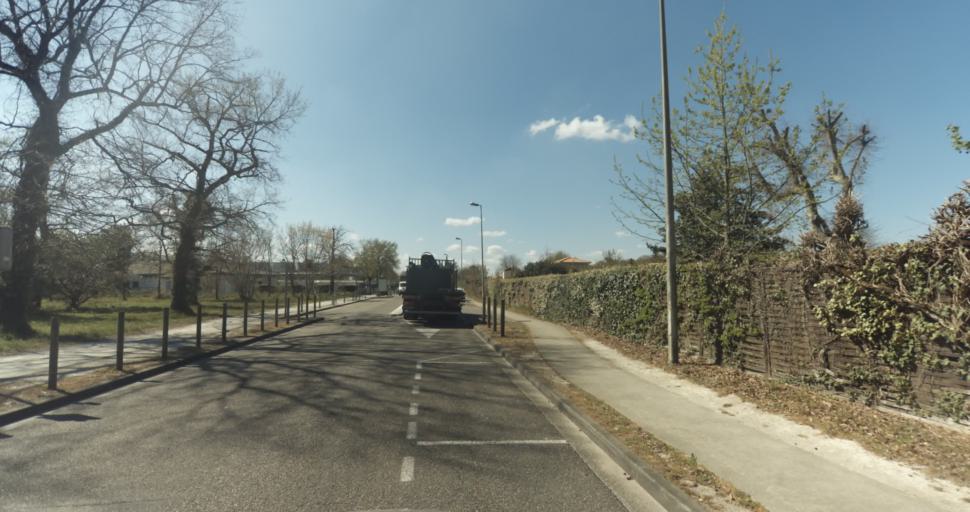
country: FR
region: Aquitaine
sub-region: Departement de la Gironde
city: Martignas-sur-Jalle
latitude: 44.8075
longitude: -0.7847
